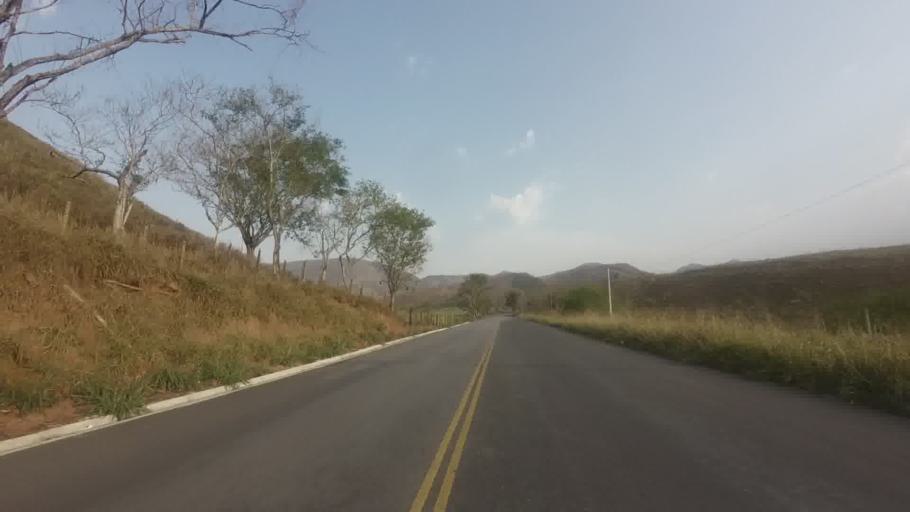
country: BR
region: Rio de Janeiro
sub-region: Cambuci
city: Cambuci
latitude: -21.4007
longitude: -41.9760
